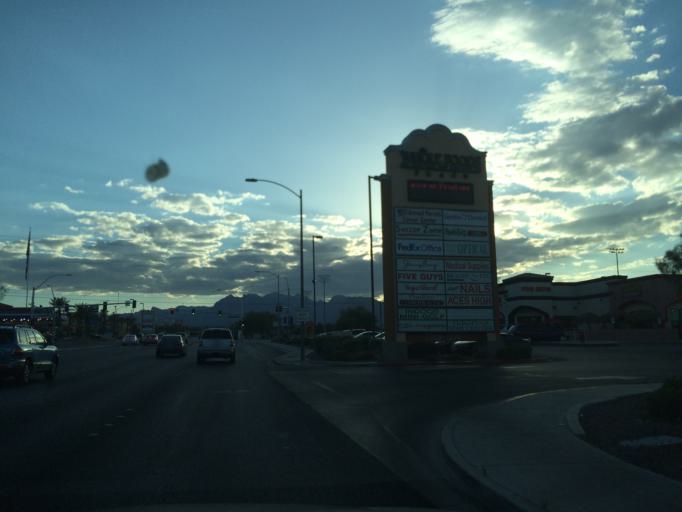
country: US
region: Nevada
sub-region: Clark County
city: Spring Valley
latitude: 36.1962
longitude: -115.2499
